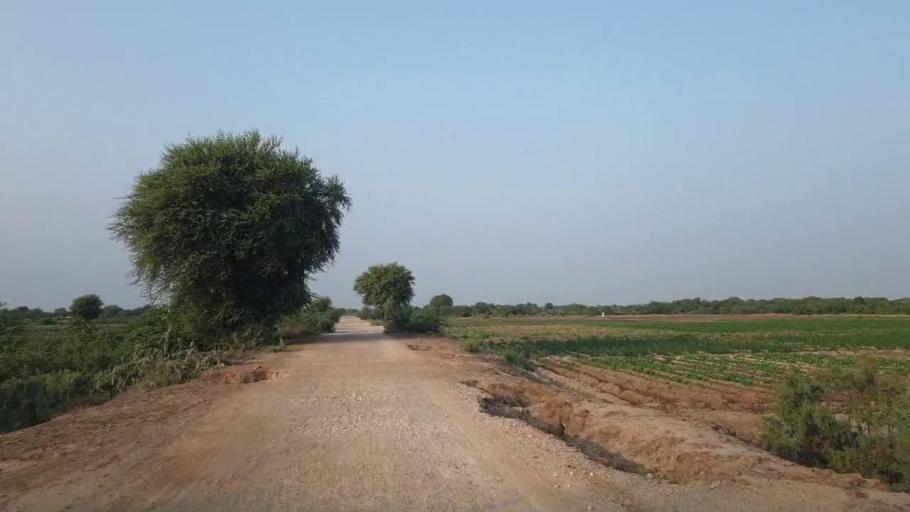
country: PK
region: Sindh
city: Rajo Khanani
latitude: 25.0307
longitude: 68.9773
